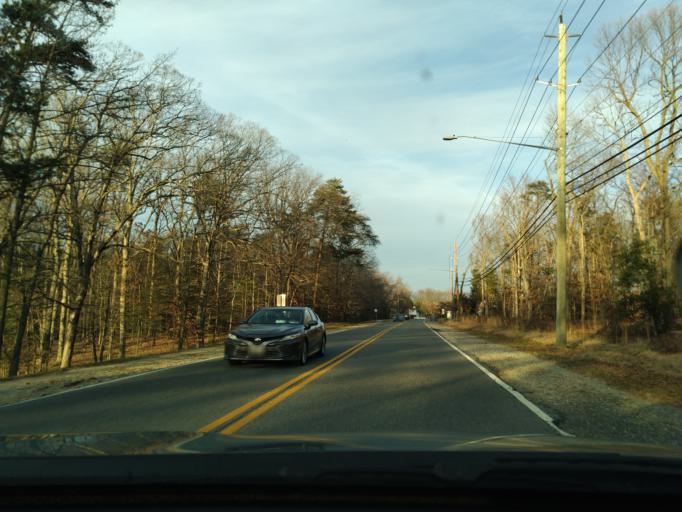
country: US
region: Maryland
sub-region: Prince George's County
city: Clinton
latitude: 38.7409
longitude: -76.9061
